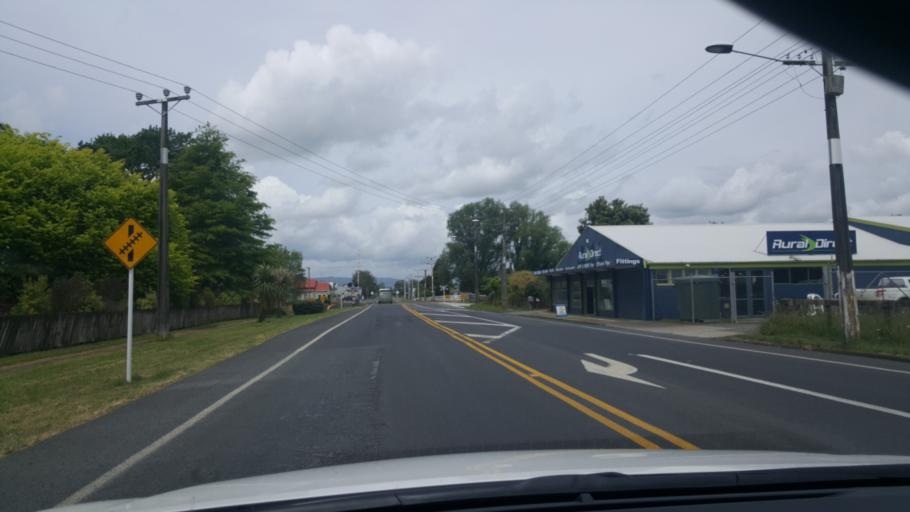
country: NZ
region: Waikato
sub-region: Matamata-Piako District
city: Matamata
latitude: -37.8816
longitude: 175.7590
